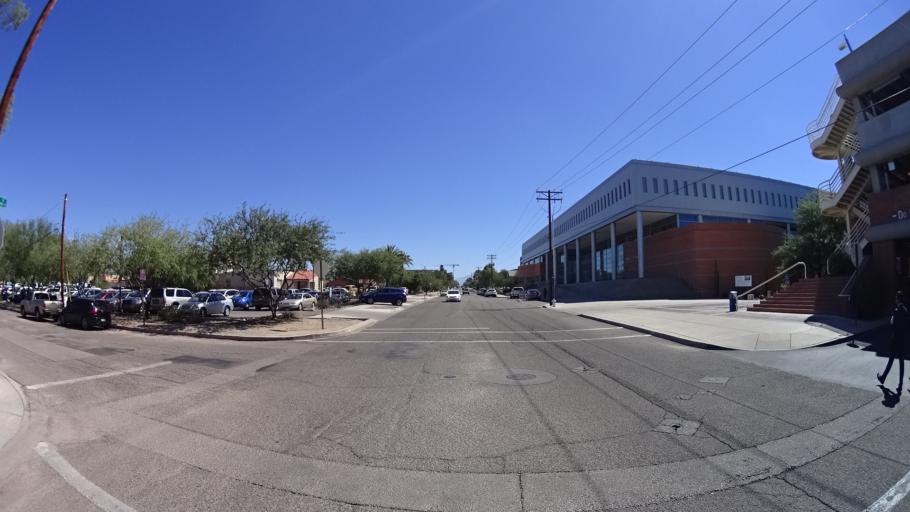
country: US
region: Arizona
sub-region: Pima County
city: Tucson
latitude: 32.2373
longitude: -110.9553
